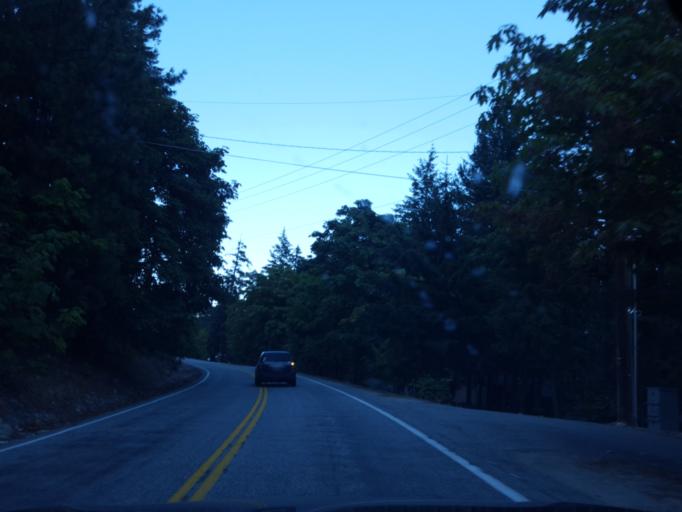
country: US
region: Washington
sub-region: Chelan County
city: Granite Falls
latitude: 47.9102
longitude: -120.2149
